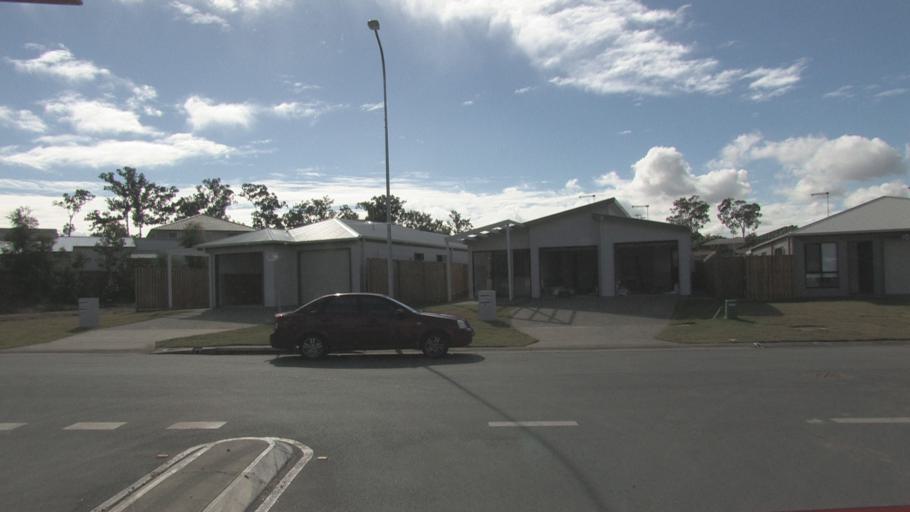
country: AU
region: Queensland
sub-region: Logan
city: Waterford West
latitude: -27.6811
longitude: 153.1296
